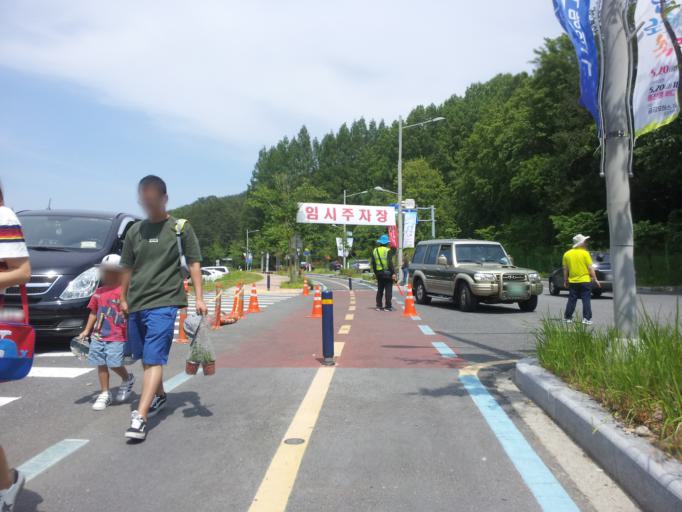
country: KR
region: Daejeon
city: Sintansin
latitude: 36.4714
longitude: 127.4742
